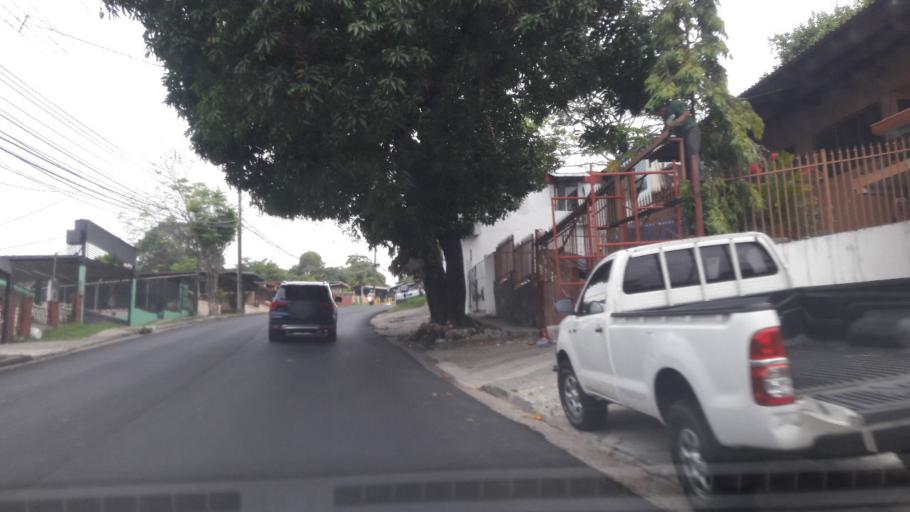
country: PA
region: Panama
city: Panama
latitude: 9.0117
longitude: -79.5276
